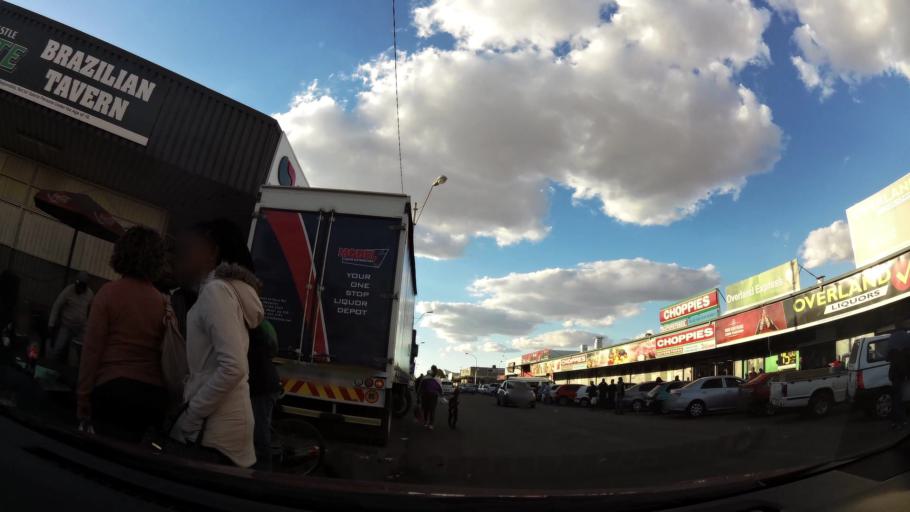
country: ZA
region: North-West
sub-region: Dr Kenneth Kaunda District Municipality
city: Potchefstroom
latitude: -26.7121
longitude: 27.1012
